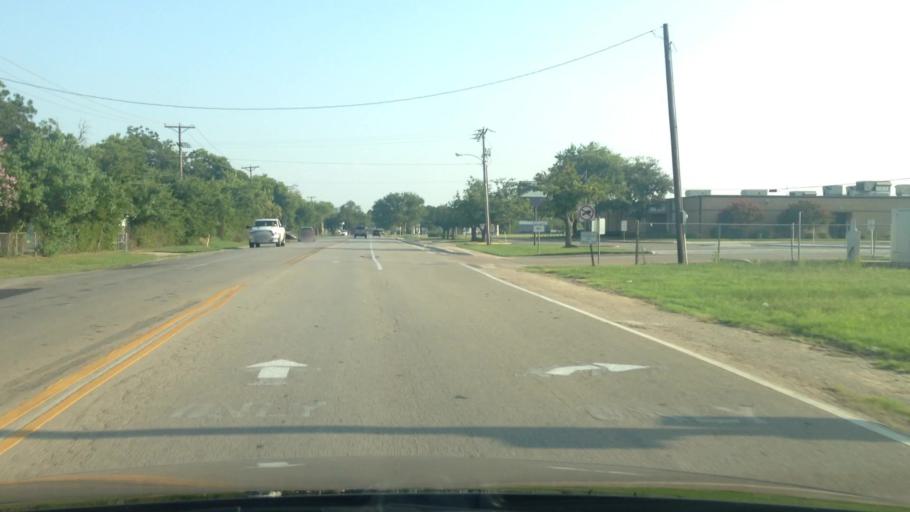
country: US
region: Texas
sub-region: Tarrant County
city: Everman
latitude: 32.6348
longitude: -97.2700
